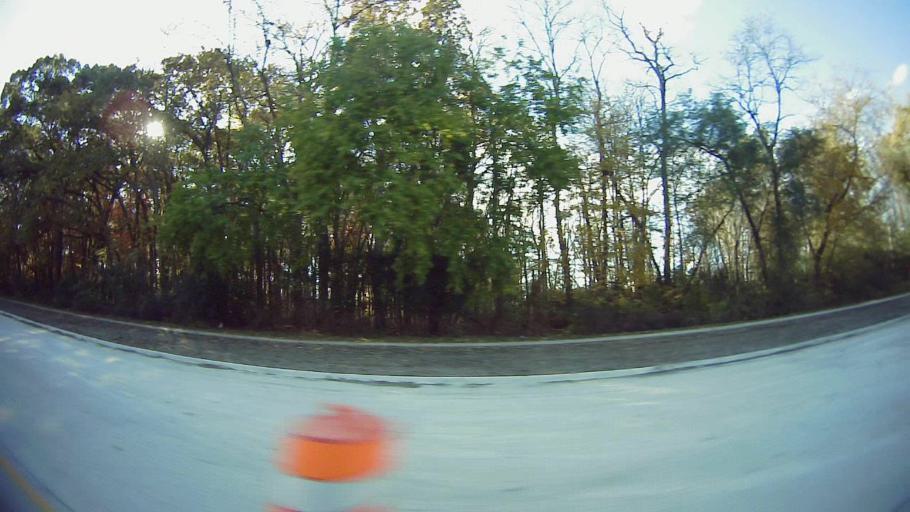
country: US
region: Michigan
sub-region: Oakland County
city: Southfield
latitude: 42.4603
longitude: -83.2399
